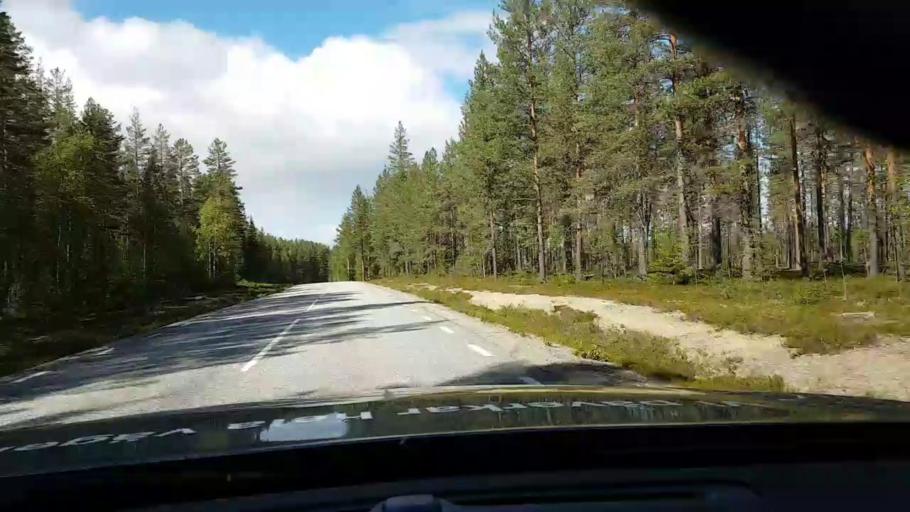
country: SE
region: Vaesternorrland
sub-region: OErnskoeldsviks Kommun
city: Bredbyn
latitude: 63.6659
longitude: 17.8334
